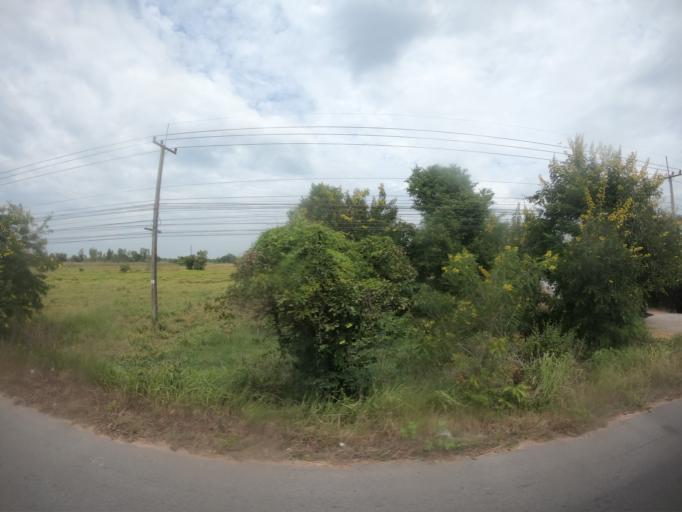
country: TH
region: Maha Sarakham
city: Maha Sarakham
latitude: 16.1591
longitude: 103.3604
